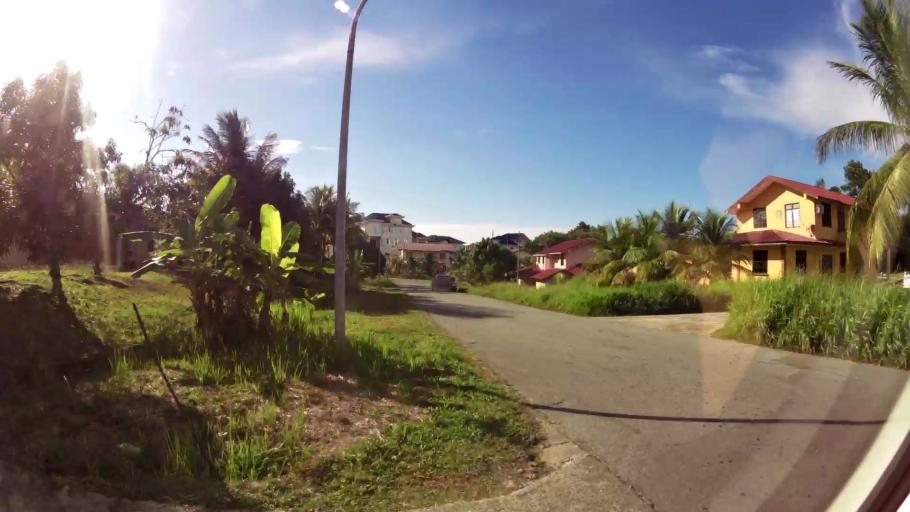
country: BN
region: Brunei and Muara
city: Bandar Seri Begawan
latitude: 4.9759
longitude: 114.9697
